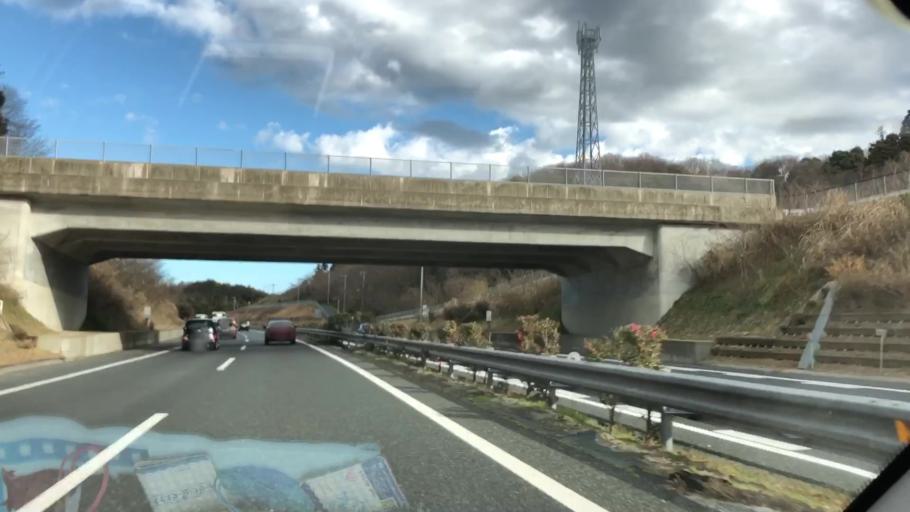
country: JP
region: Chiba
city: Kisarazu
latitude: 35.3259
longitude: 139.9461
